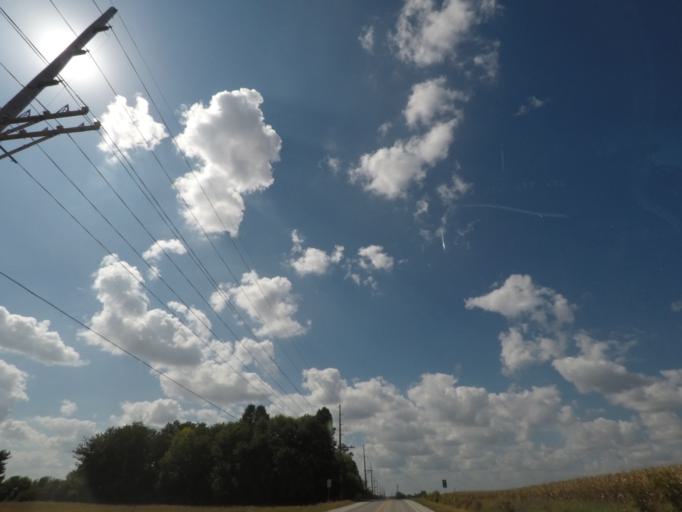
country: US
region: Iowa
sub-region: Story County
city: Ames
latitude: 42.0230
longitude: -93.5480
